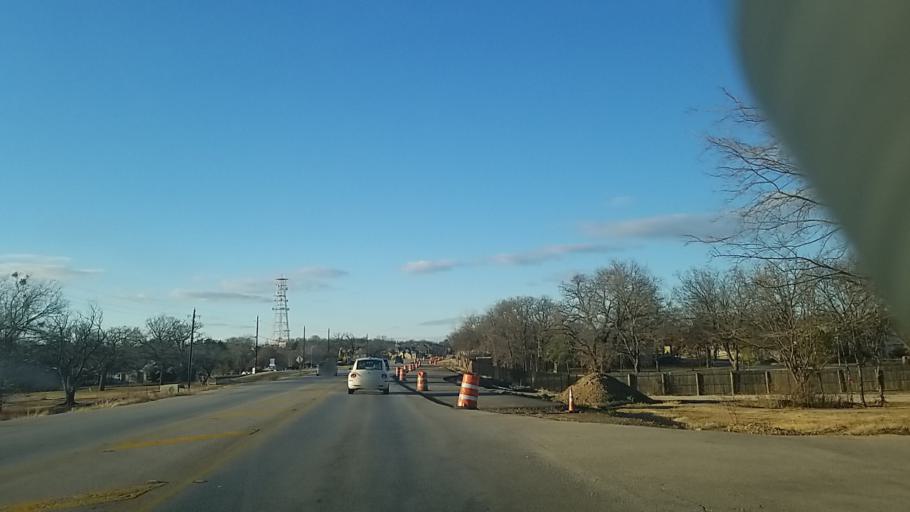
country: US
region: Texas
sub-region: Denton County
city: Corinth
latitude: 33.1627
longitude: -97.1075
